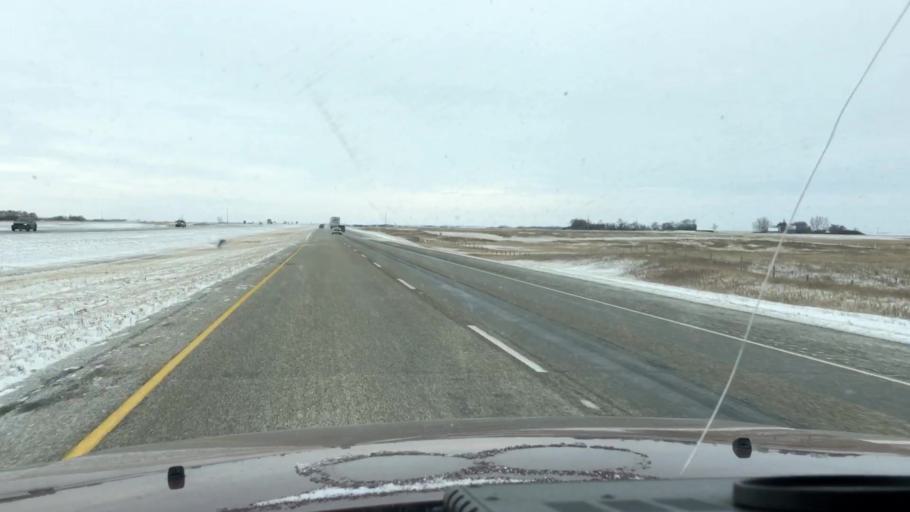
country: CA
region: Saskatchewan
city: Saskatoon
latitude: 51.6259
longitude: -106.4229
